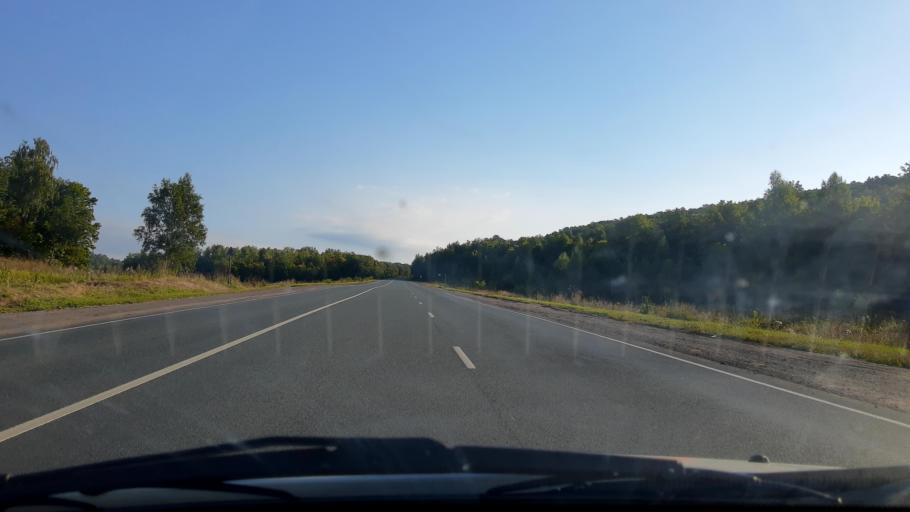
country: RU
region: Bashkortostan
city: Oktyabr'skiy
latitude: 54.4341
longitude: 53.4955
